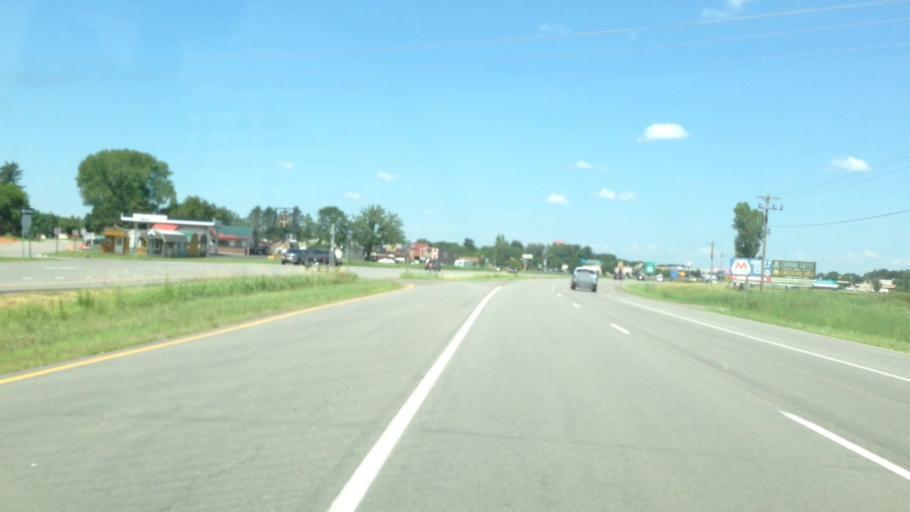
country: US
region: Minnesota
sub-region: Sherburne County
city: Zimmerman
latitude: 45.4375
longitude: -93.5814
